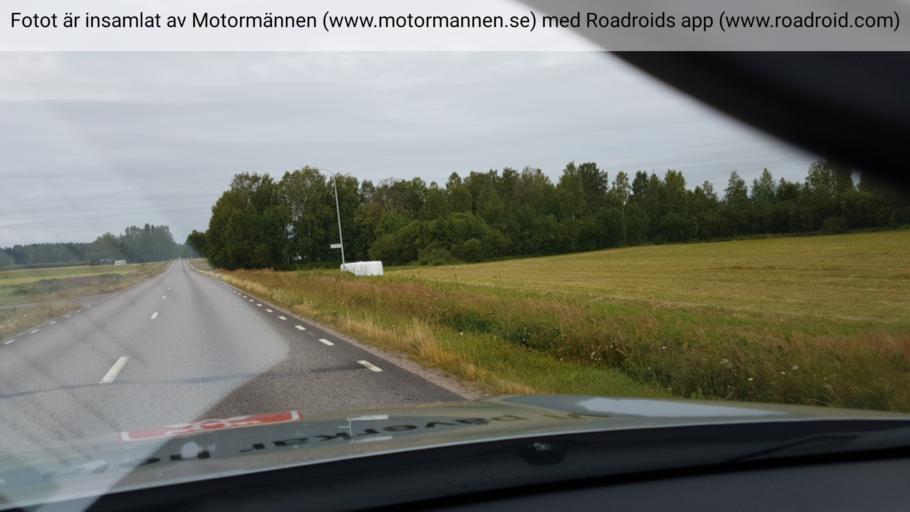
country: SE
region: Norrbotten
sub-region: Lulea Kommun
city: Sodra Sunderbyn
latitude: 65.6521
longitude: 21.8639
